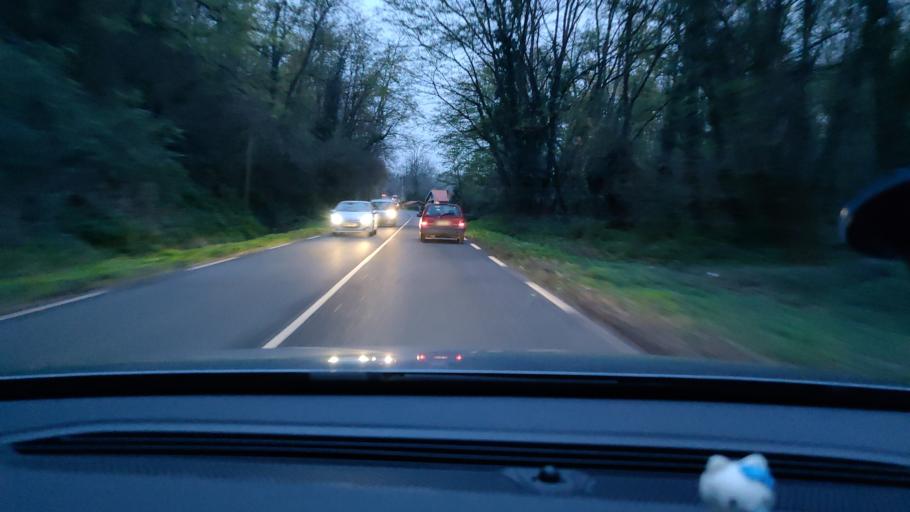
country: FR
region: Midi-Pyrenees
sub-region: Departement de la Haute-Garonne
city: Vieille-Toulouse
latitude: 43.5421
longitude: 1.4361
